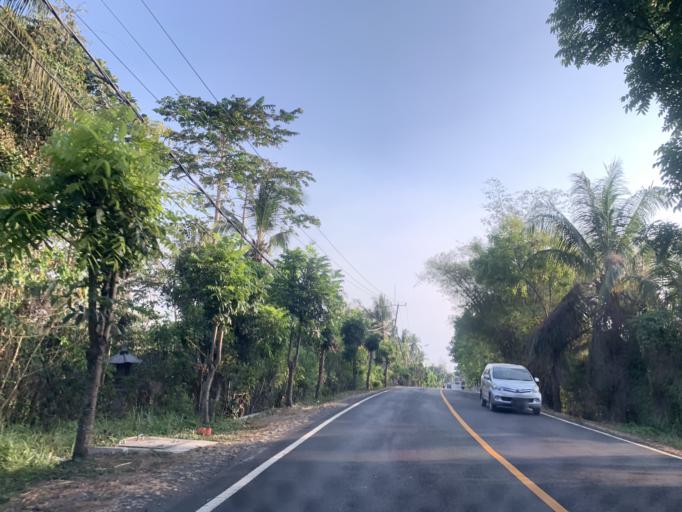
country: ID
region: Bali
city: Banjar Delodrurung
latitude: -8.5102
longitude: 115.0173
